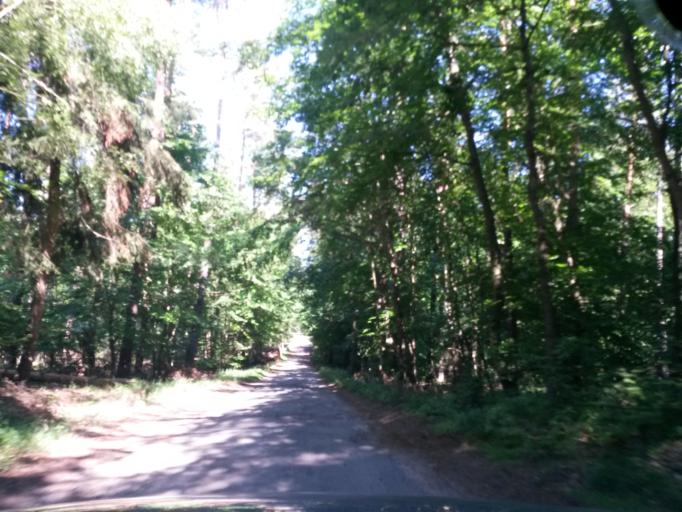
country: DE
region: Brandenburg
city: Templin
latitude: 53.2038
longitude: 13.4547
